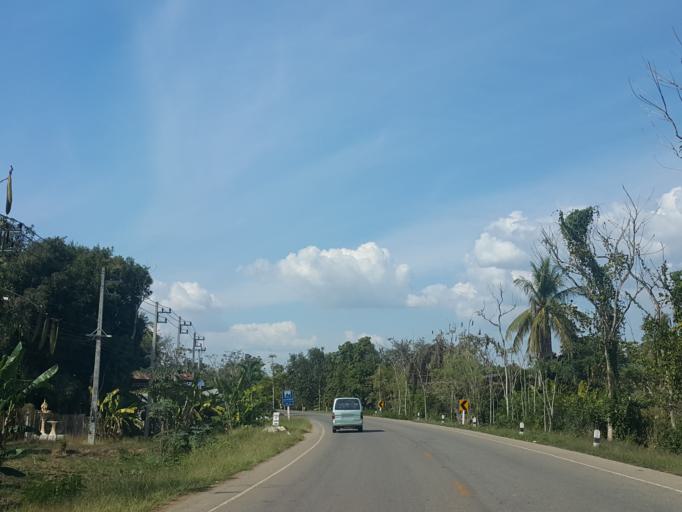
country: TH
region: Sukhothai
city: Sawankhalok
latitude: 17.2635
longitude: 99.8357
